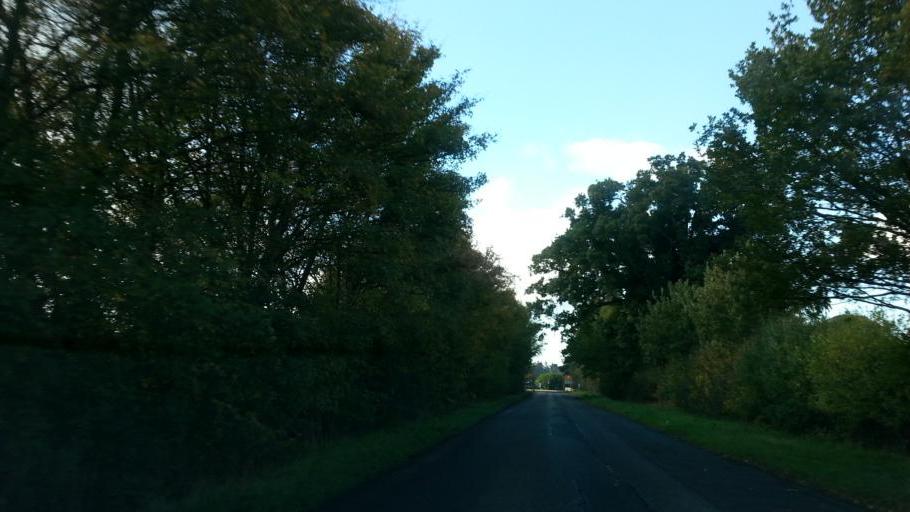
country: GB
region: England
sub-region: Suffolk
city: Thurston
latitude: 52.2345
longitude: 0.8017
